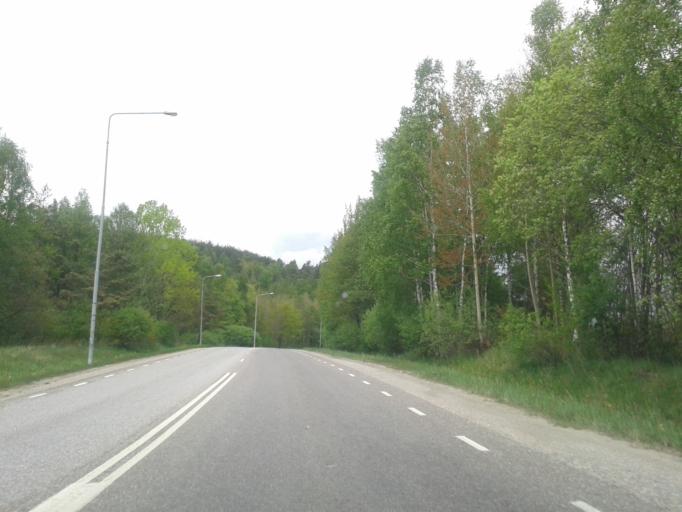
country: SE
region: Vaestra Goetaland
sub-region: Goteborg
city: Eriksbo
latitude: 57.7745
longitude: 12.0498
